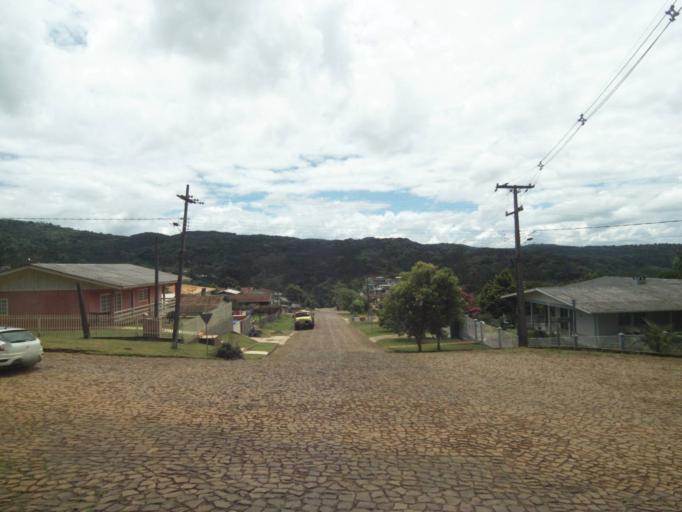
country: BR
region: Parana
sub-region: Pinhao
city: Pinhao
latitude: -26.1597
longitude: -51.5579
